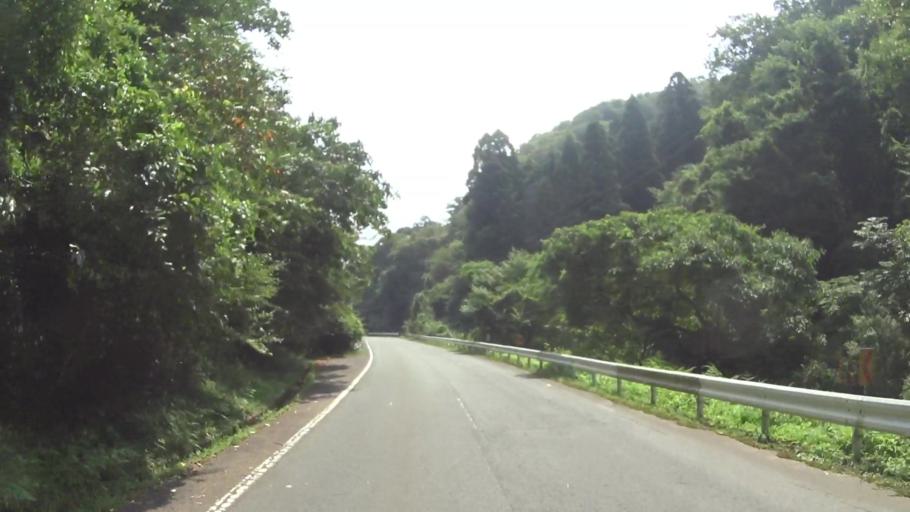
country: JP
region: Kyoto
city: Ayabe
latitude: 35.2013
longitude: 135.3759
